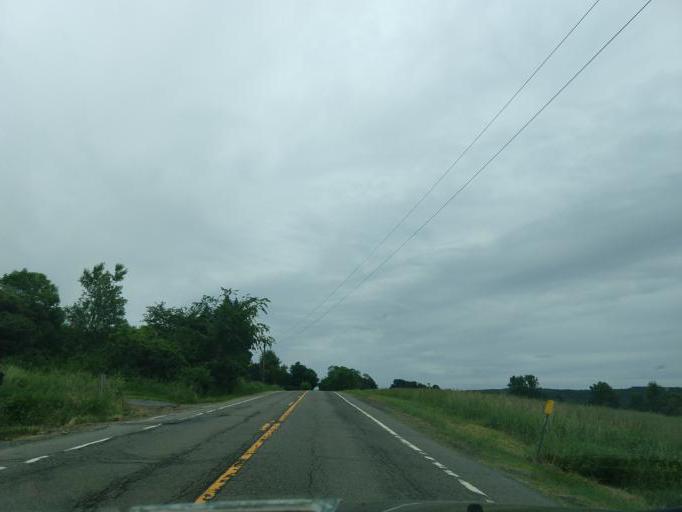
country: US
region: New York
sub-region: Tompkins County
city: Dryden
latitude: 42.4894
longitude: -76.2677
